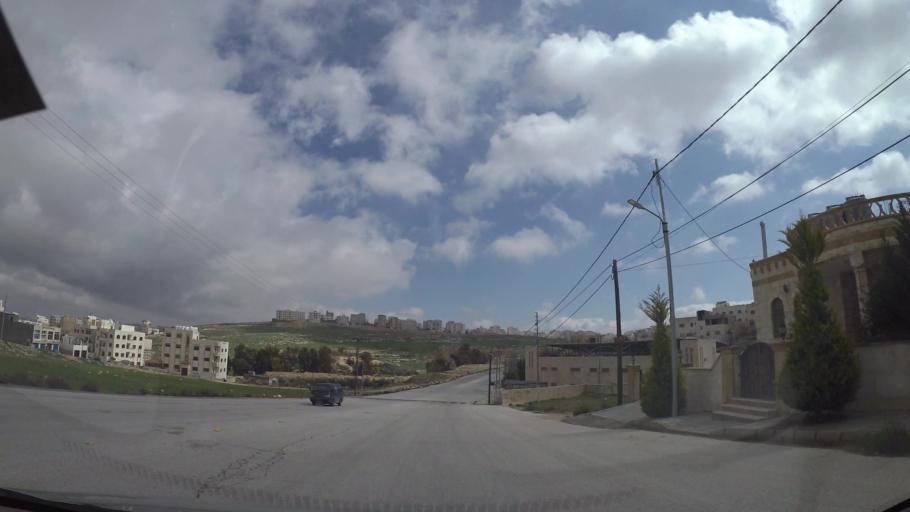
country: JO
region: Amman
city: Al Jubayhah
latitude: 32.0710
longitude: 35.8835
